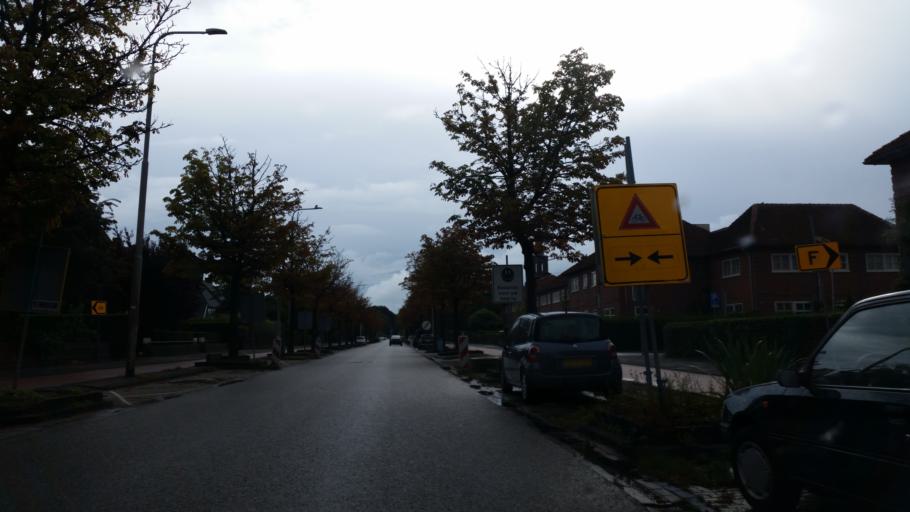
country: NL
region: Friesland
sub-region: Gemeente Leeuwarden
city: Bilgaard
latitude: 53.2047
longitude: 5.7789
